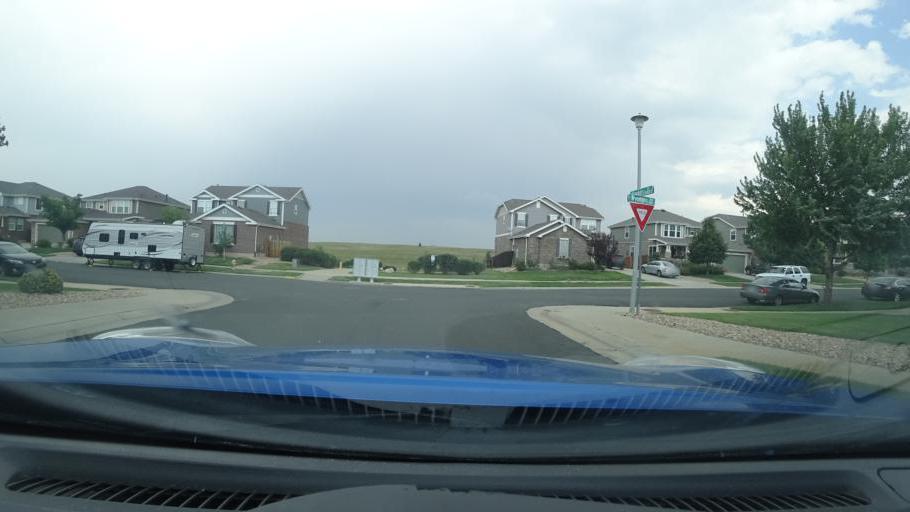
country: US
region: Colorado
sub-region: Adams County
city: Aurora
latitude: 39.6913
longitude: -104.7603
